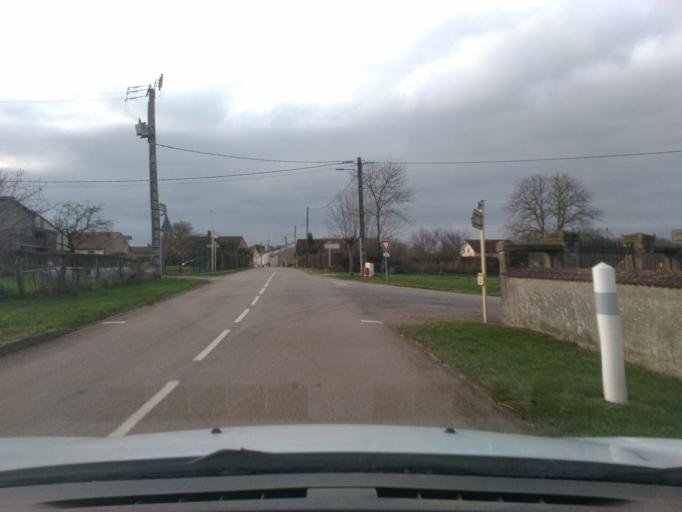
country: FR
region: Lorraine
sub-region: Departement des Vosges
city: Mirecourt
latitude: 48.3357
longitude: 6.0248
